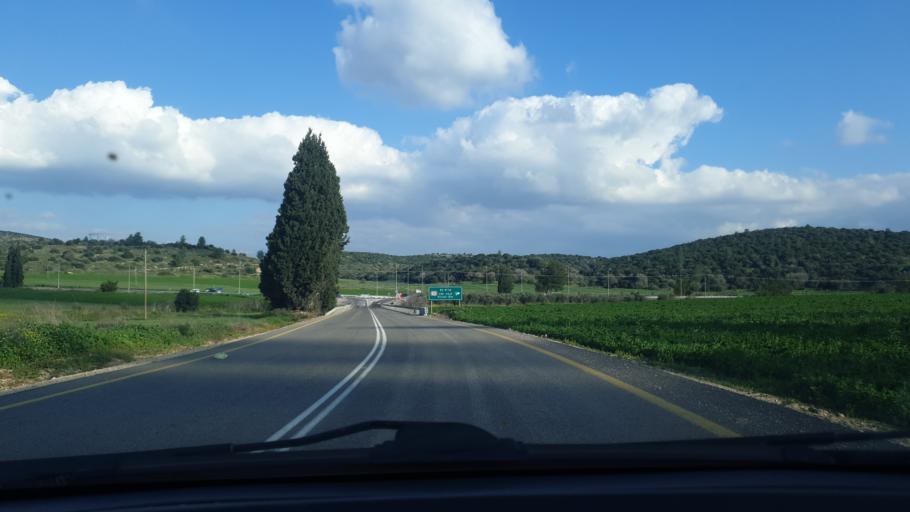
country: IL
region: Jerusalem
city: Bet Shemesh
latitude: 31.7029
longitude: 34.9405
